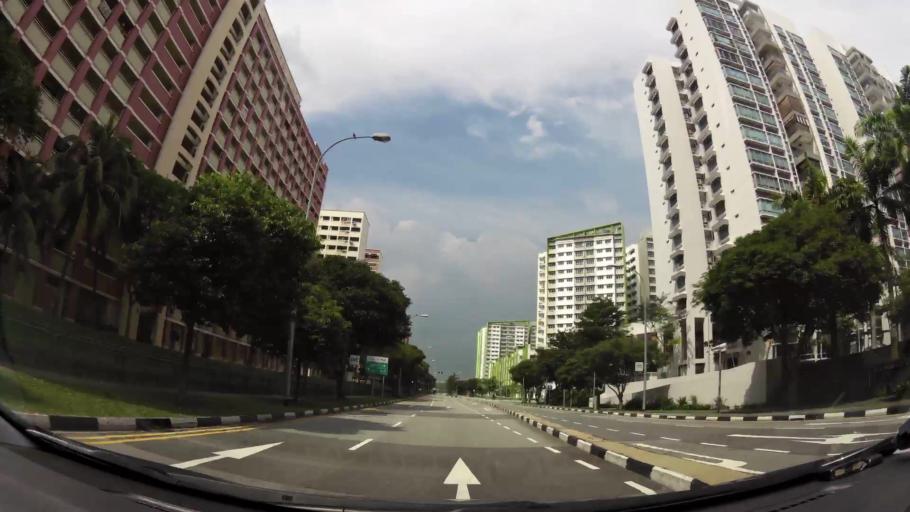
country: SG
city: Singapore
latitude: 1.3566
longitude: 103.9381
